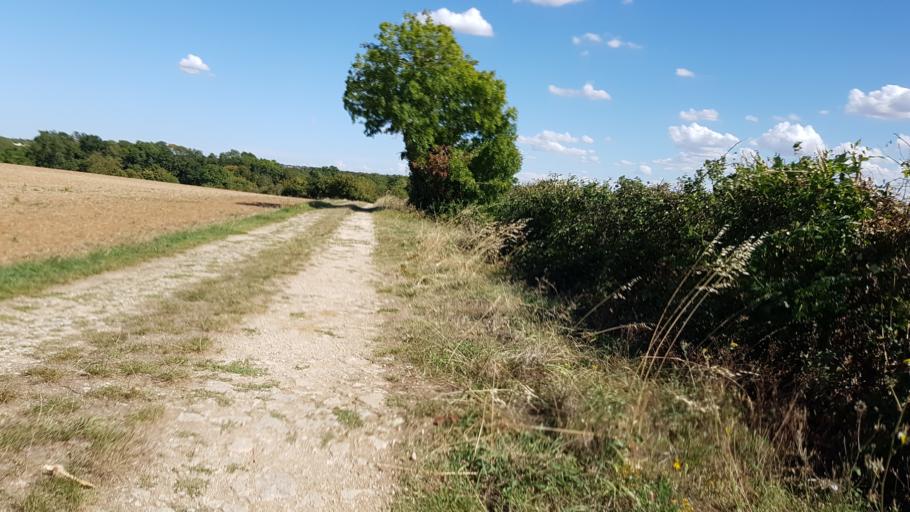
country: FR
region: Poitou-Charentes
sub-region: Departement des Deux-Sevres
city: Vouille
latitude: 46.3209
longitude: -0.3677
